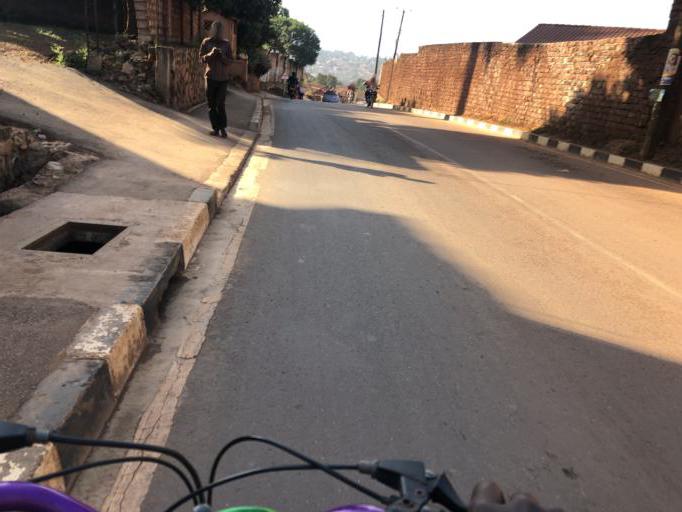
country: UG
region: Central Region
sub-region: Kampala District
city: Kampala
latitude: 0.2789
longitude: 32.5984
